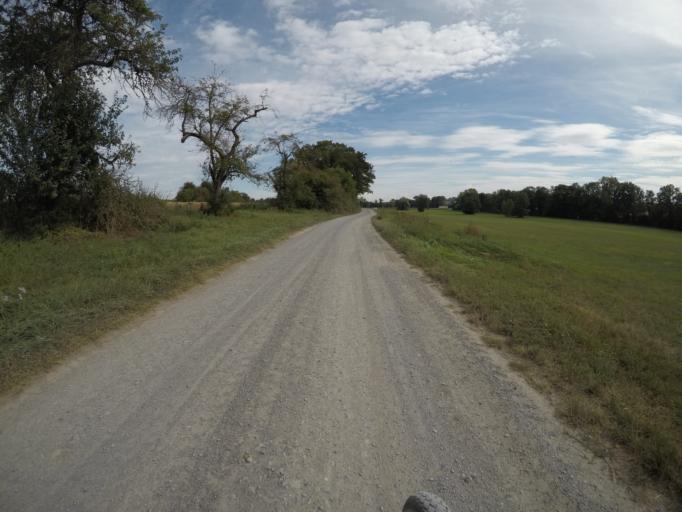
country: DE
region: Baden-Wuerttemberg
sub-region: Karlsruhe Region
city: Illingen
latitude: 48.9631
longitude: 8.9019
